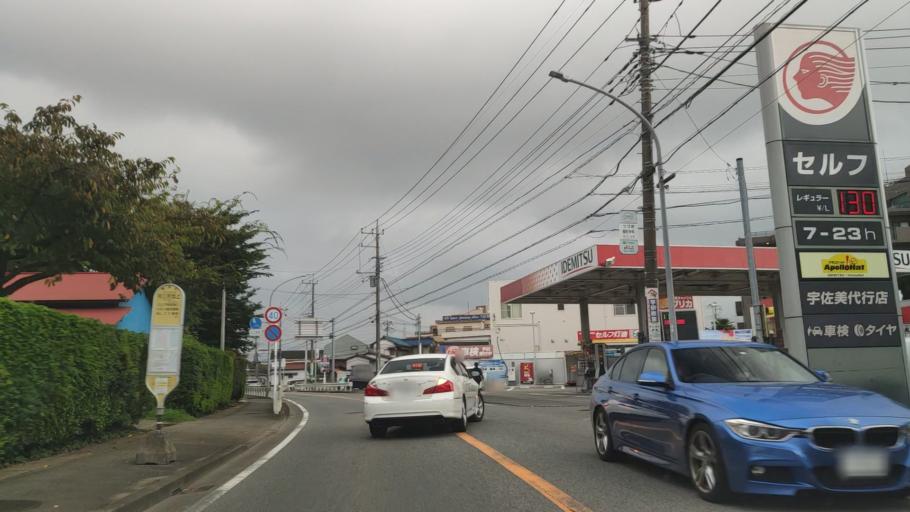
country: JP
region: Kanagawa
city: Minami-rinkan
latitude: 35.4459
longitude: 139.4999
